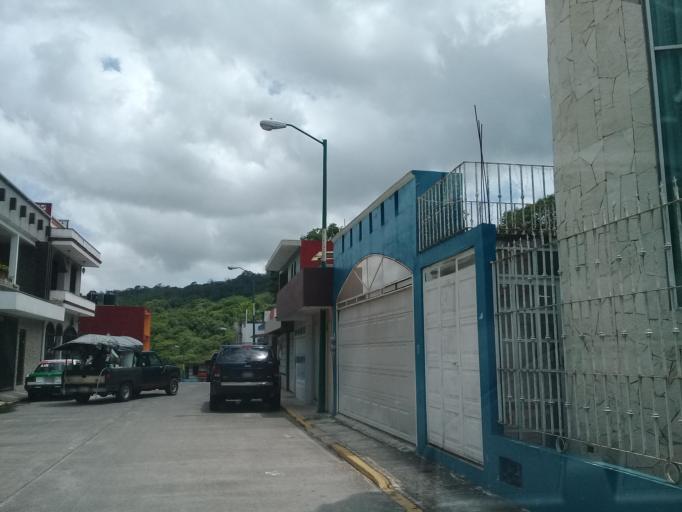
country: MX
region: Veracruz
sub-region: Xalapa
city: Lomas Verdes
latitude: 19.5035
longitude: -96.8914
